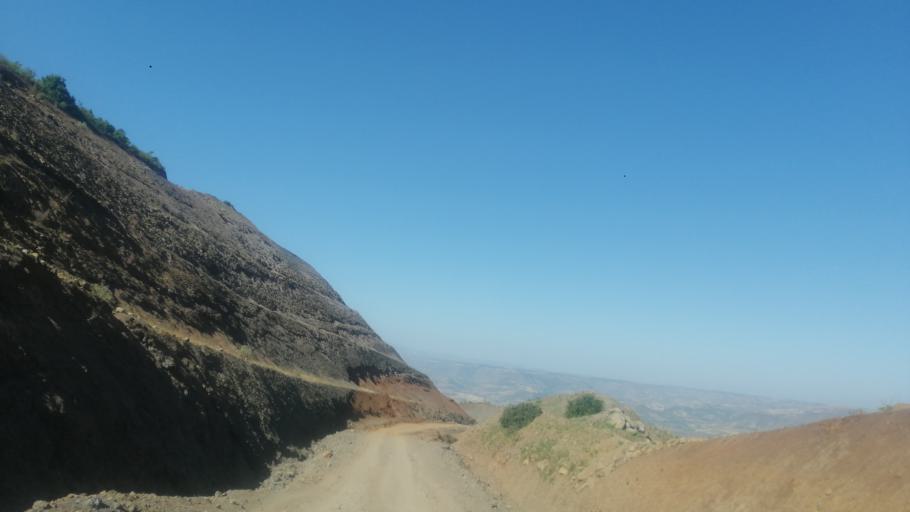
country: ET
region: Amhara
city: Addiet Canna
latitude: 11.1529
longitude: 37.8548
